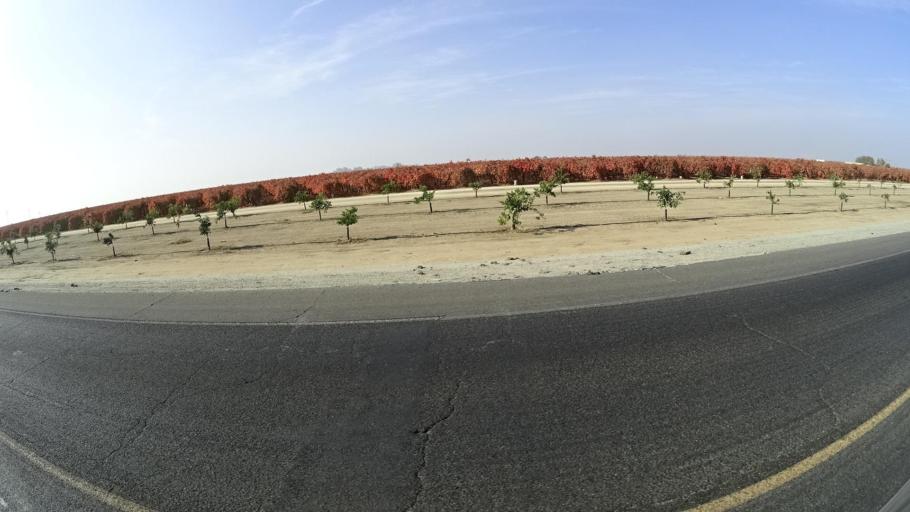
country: US
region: California
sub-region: Tulare County
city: Richgrove
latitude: 35.7383
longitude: -119.1473
